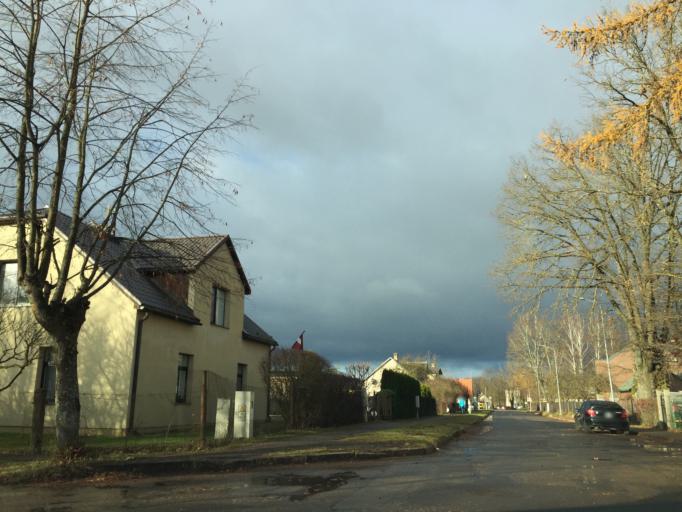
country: LV
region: Valmieras Rajons
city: Valmiera
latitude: 57.5316
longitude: 25.3995
